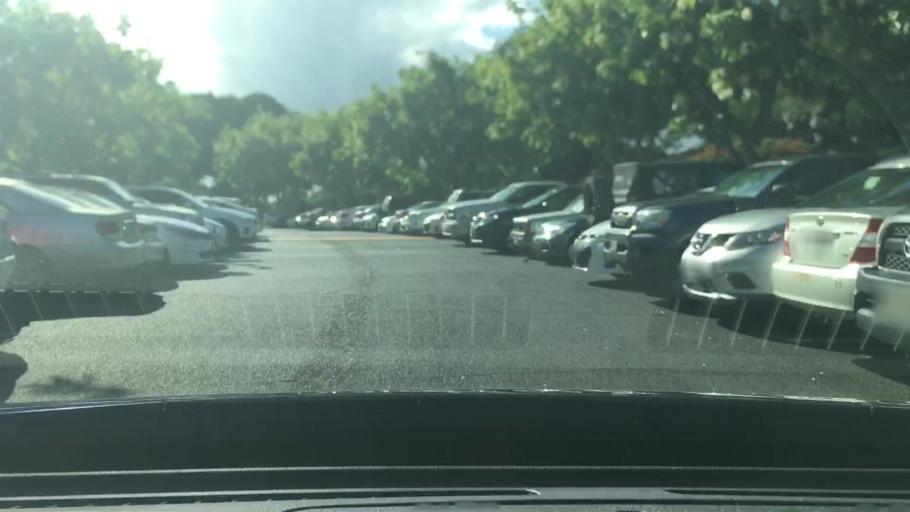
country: US
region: Hawaii
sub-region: Honolulu County
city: Honolulu
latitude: 21.2702
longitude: -157.8027
